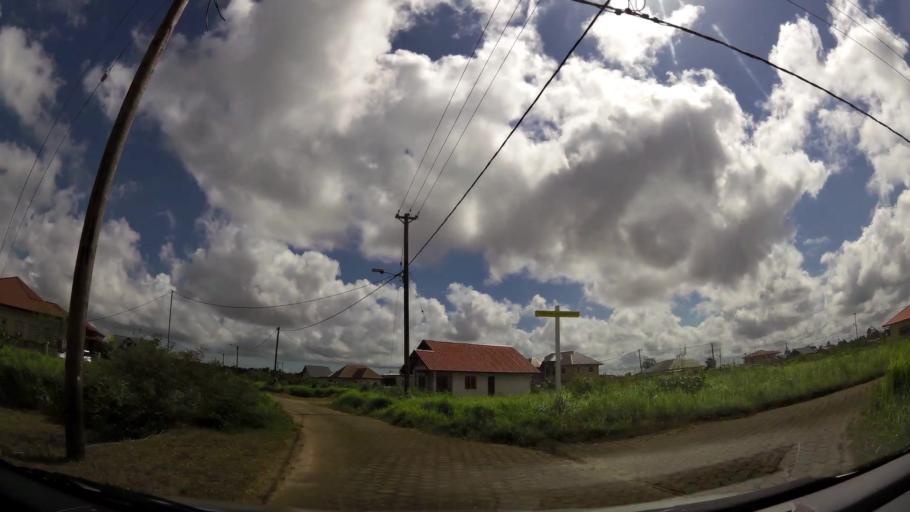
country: SR
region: Paramaribo
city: Paramaribo
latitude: 5.8755
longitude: -55.1290
